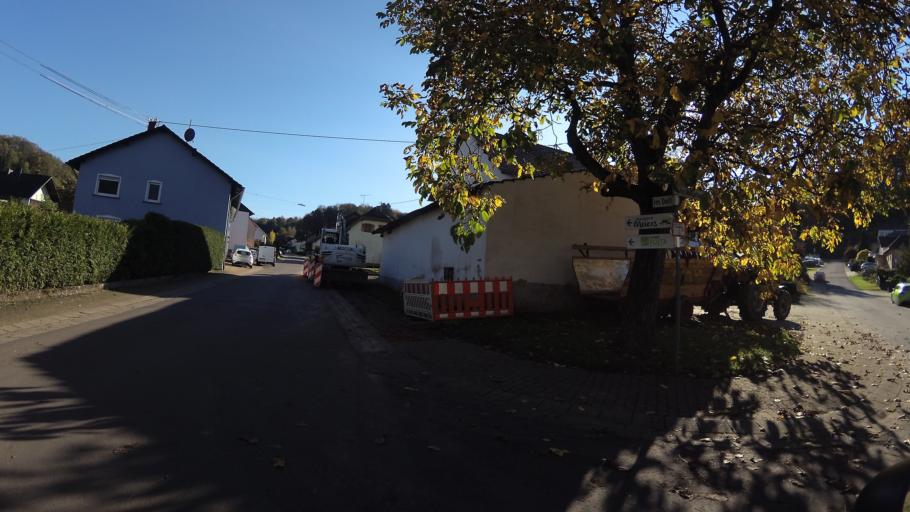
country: DE
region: Saarland
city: Losheim
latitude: 49.4719
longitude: 6.7244
